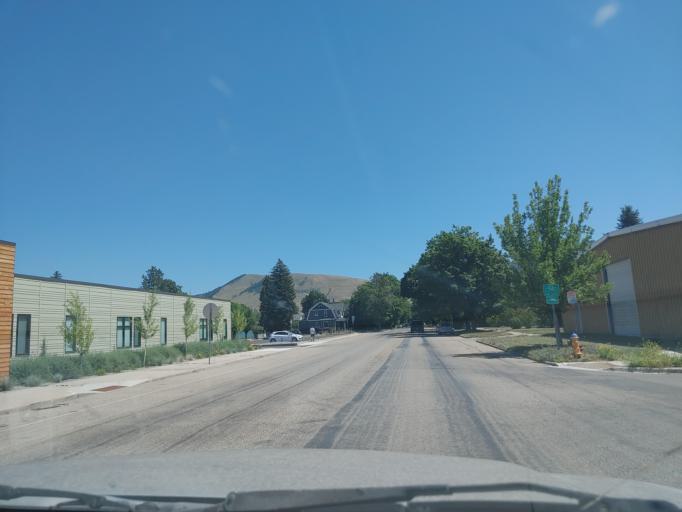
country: US
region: Montana
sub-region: Missoula County
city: Missoula
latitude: 46.8670
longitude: -114.0097
